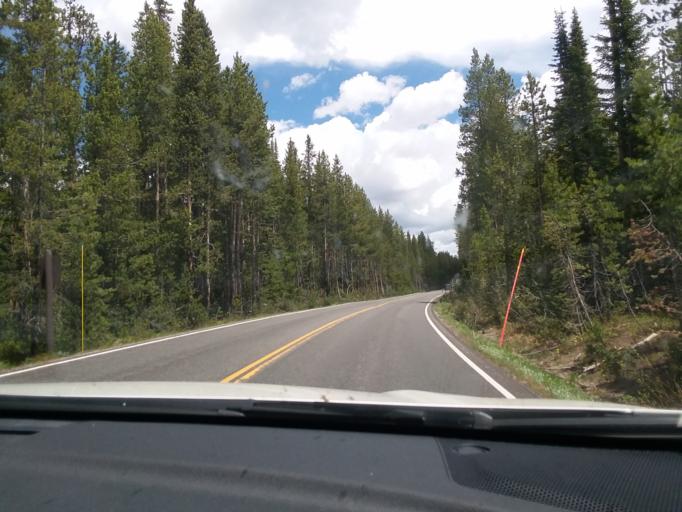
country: US
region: Idaho
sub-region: Teton County
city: Driggs
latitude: 44.1548
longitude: -110.6745
